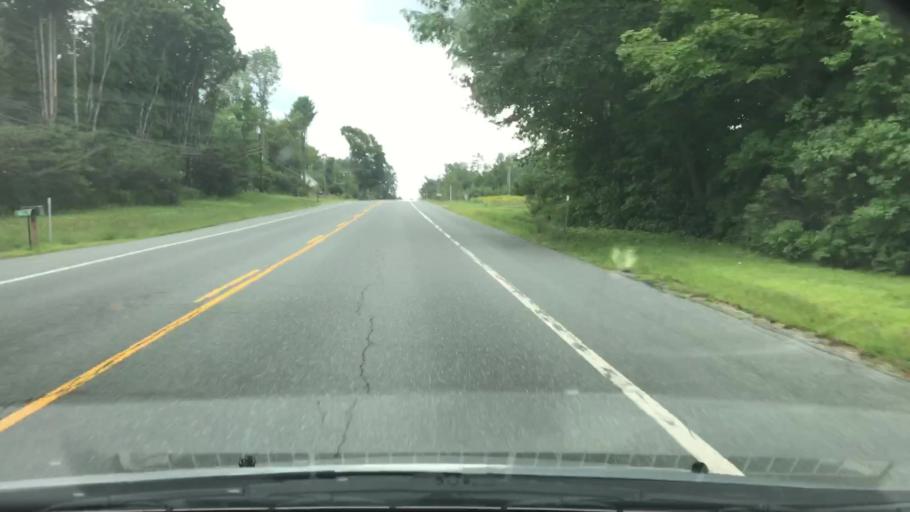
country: US
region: New Hampshire
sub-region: Grafton County
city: Lyme
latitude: 43.7976
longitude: -72.1689
